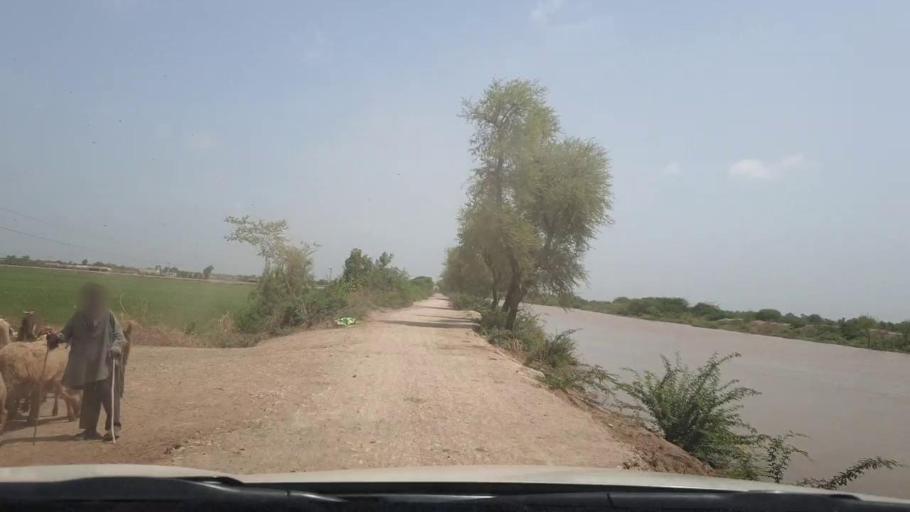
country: PK
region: Sindh
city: Talhar
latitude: 24.9201
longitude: 68.8394
